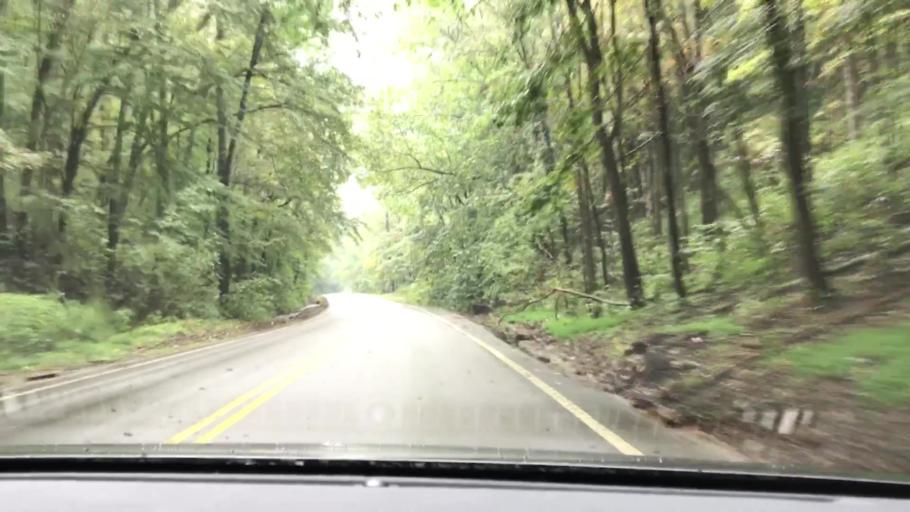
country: US
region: Tennessee
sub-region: Macon County
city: Red Boiling Springs
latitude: 36.4241
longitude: -85.9181
